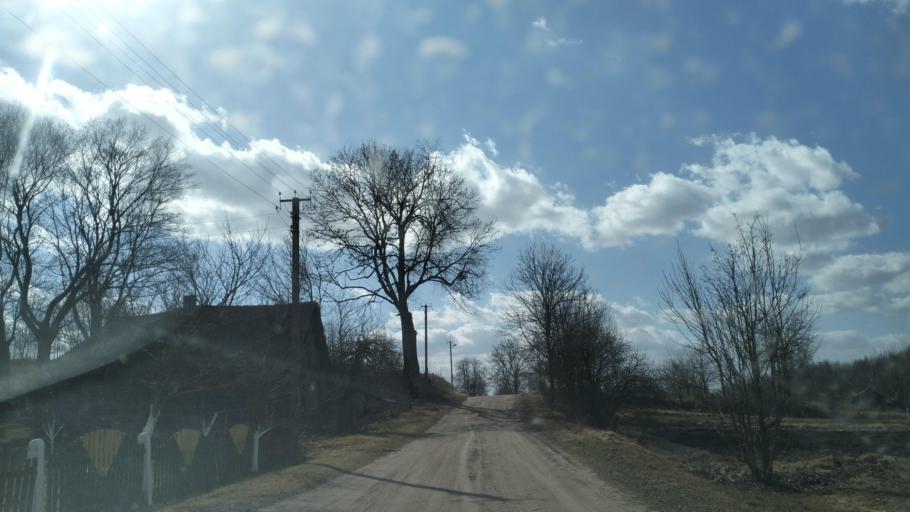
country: BY
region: Grodnenskaya
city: Karelichy
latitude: 53.6544
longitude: 26.0984
